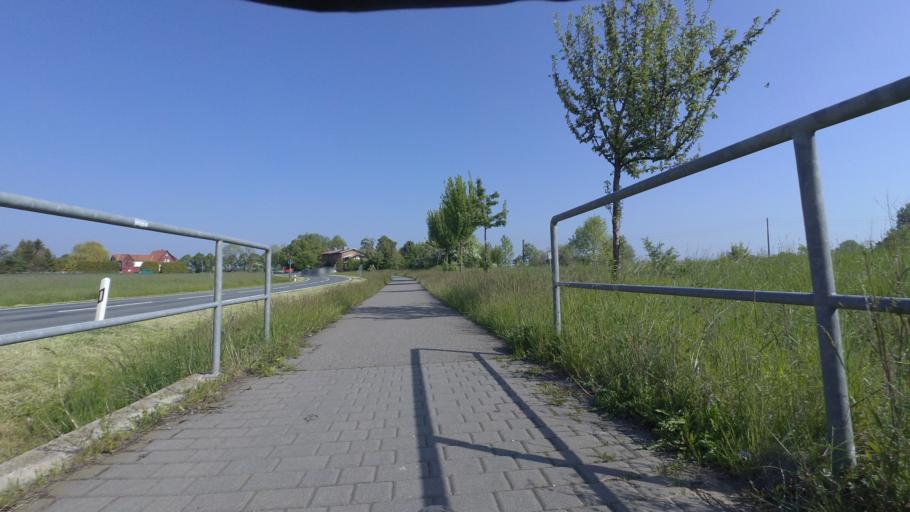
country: DE
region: Saxony-Anhalt
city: Darlingerode
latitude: 51.8522
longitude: 10.7287
